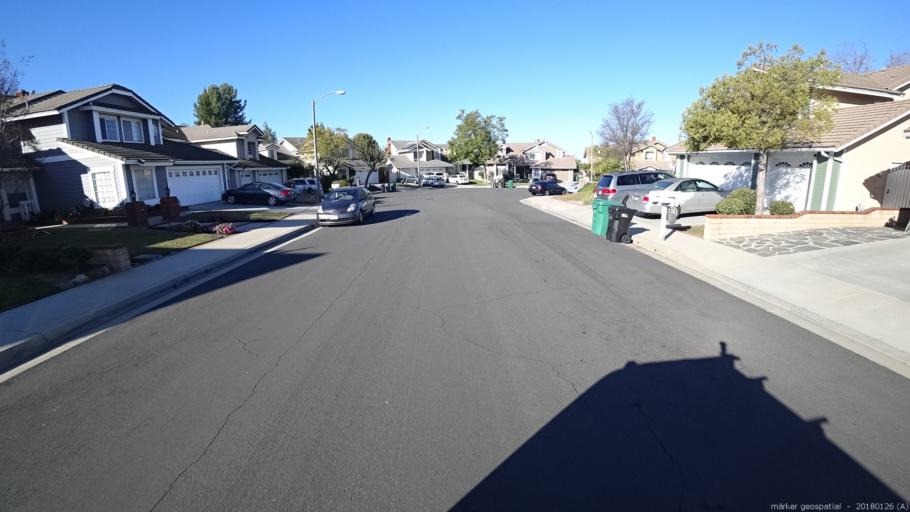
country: US
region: California
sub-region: Los Angeles County
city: Walnut
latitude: 33.9806
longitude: -117.8538
